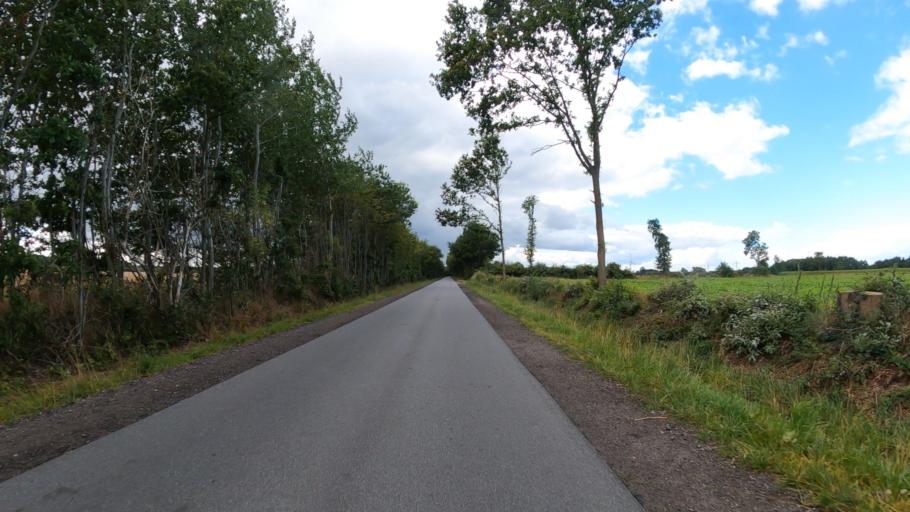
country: DE
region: Schleswig-Holstein
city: Padenstedt
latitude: 54.0302
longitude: 9.9201
